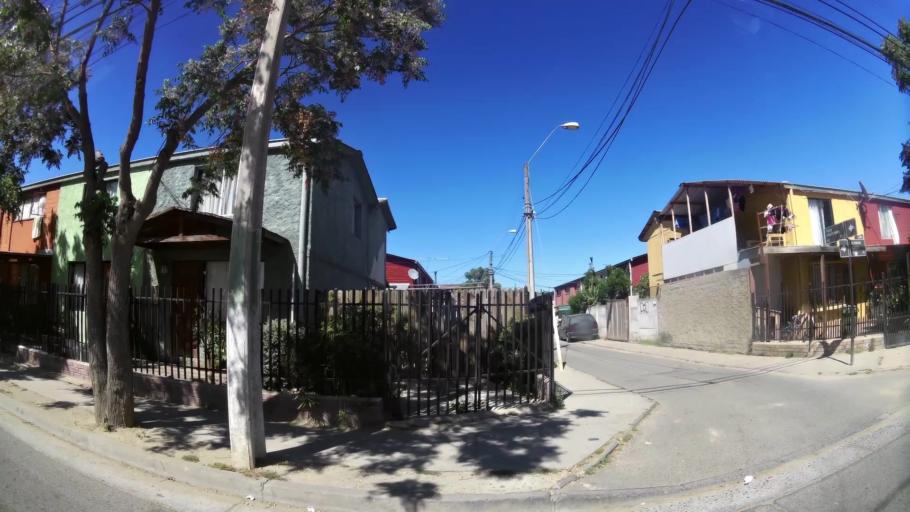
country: CL
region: Valparaiso
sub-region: Provincia de Marga Marga
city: Quilpue
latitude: -33.3073
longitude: -71.4116
